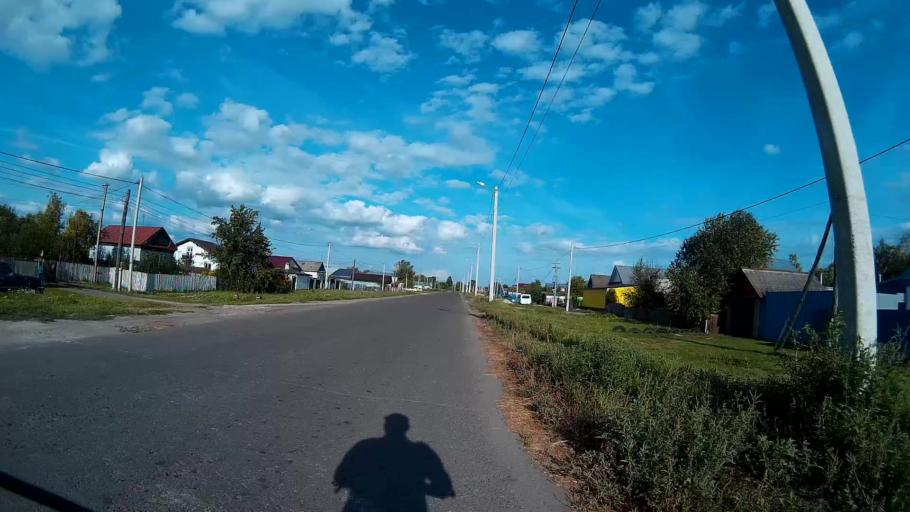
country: RU
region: Ulyanovsk
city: Isheyevka
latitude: 54.2900
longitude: 48.1970
